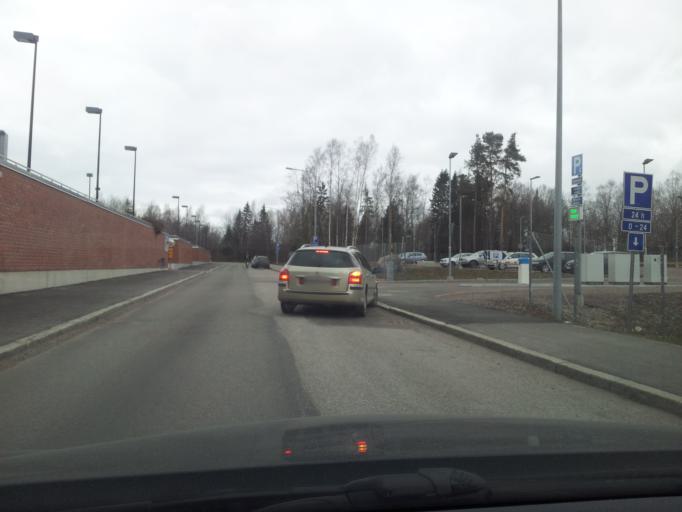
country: FI
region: Uusimaa
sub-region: Helsinki
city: Otaniemi
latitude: 60.1879
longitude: 24.8101
